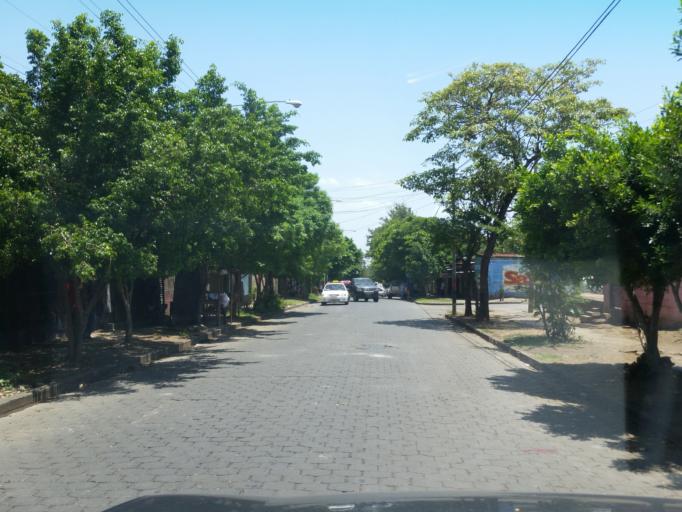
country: NI
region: Managua
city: Managua
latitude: 12.1132
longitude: -86.2339
